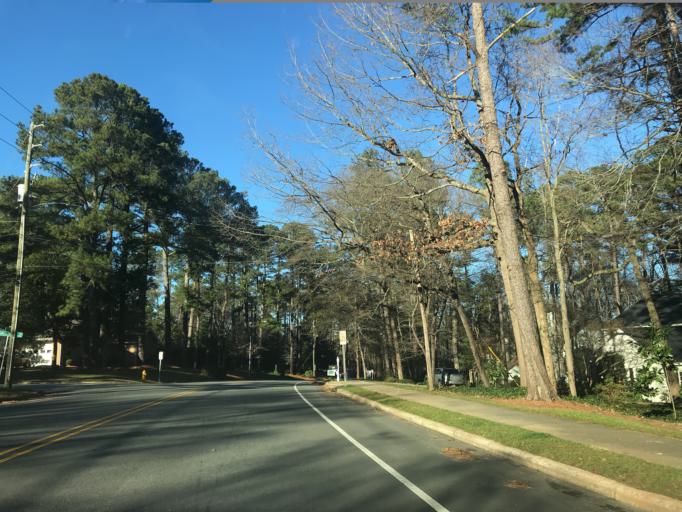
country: US
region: North Carolina
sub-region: Wake County
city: West Raleigh
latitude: 35.8258
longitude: -78.6771
